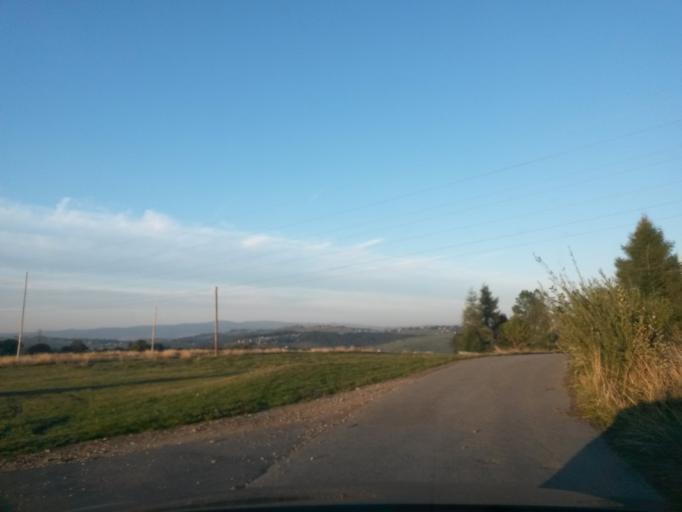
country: PL
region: Lesser Poland Voivodeship
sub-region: Powiat tatrzanski
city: Koscielisko
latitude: 49.3198
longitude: 19.9030
